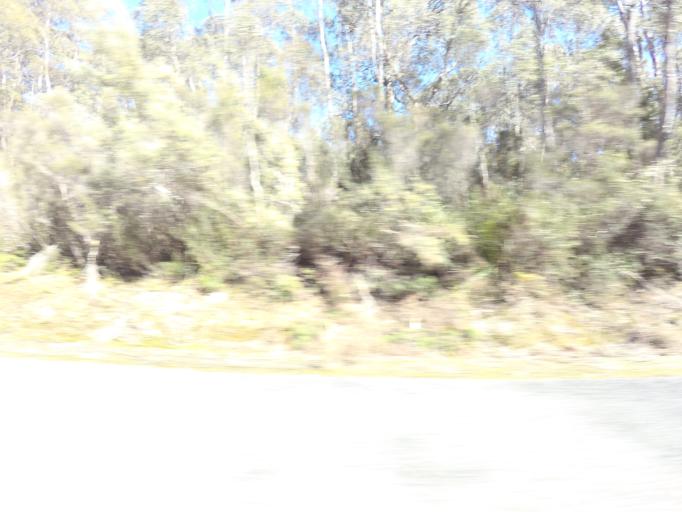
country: AU
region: Tasmania
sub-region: Derwent Valley
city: New Norfolk
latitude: -42.7528
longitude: 146.4109
